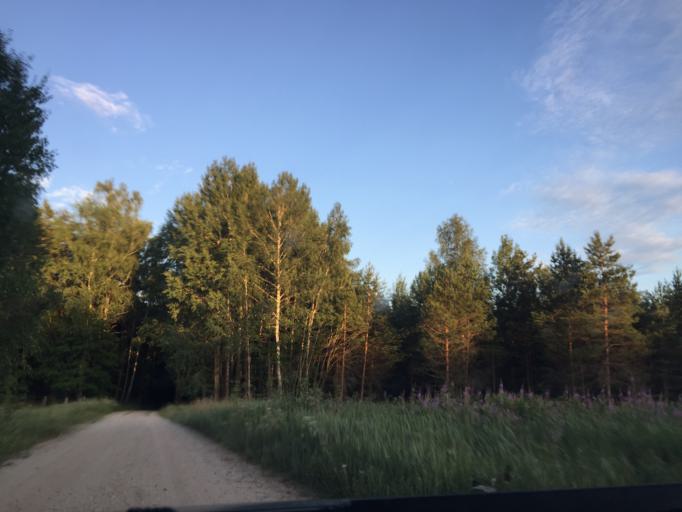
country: LV
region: Koknese
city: Koknese
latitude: 56.6206
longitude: 25.4925
